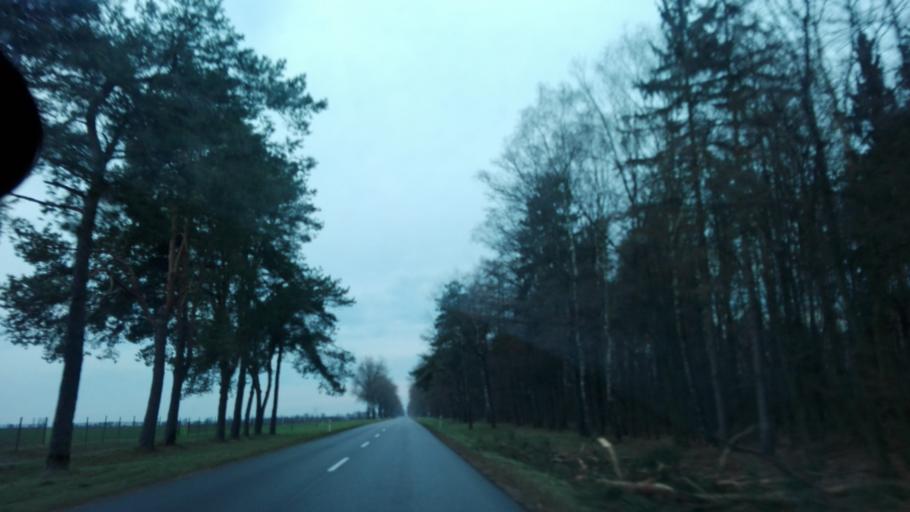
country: PL
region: Lublin Voivodeship
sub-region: Powiat radzynski
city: Wohyn
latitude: 51.7783
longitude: 22.8289
